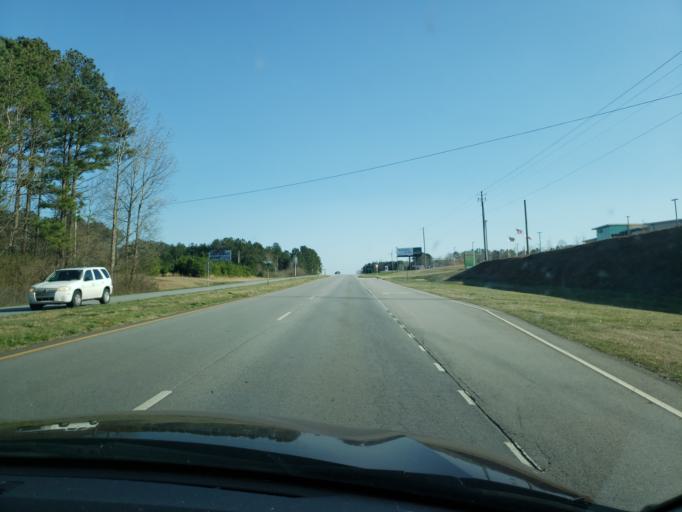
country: US
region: Alabama
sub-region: Randolph County
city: Wedowee
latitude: 33.2972
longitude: -85.4805
